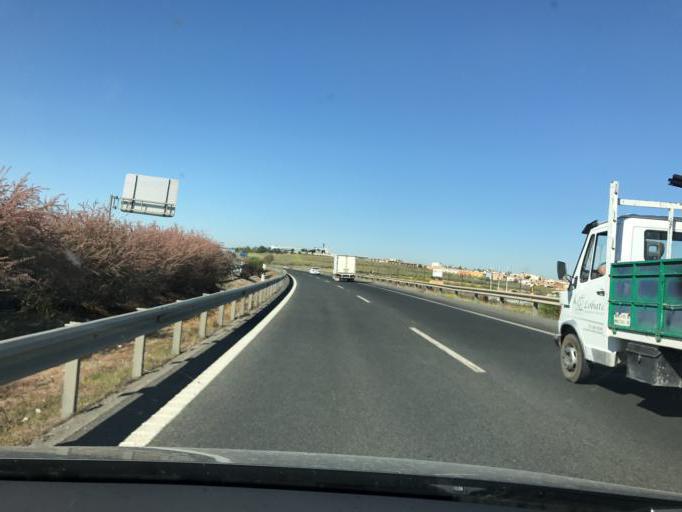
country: ES
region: Andalusia
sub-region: Provincia de Granada
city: Cijuela
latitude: 37.1948
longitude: -3.8177
